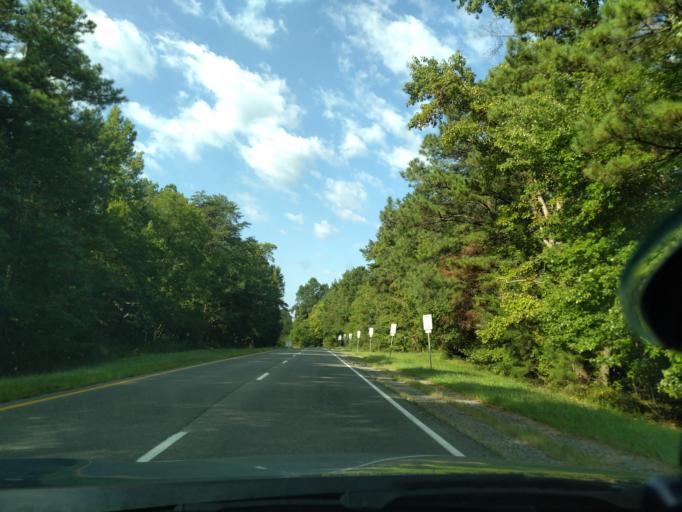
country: US
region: Virginia
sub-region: King George County
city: King George
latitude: 38.1433
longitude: -77.2248
